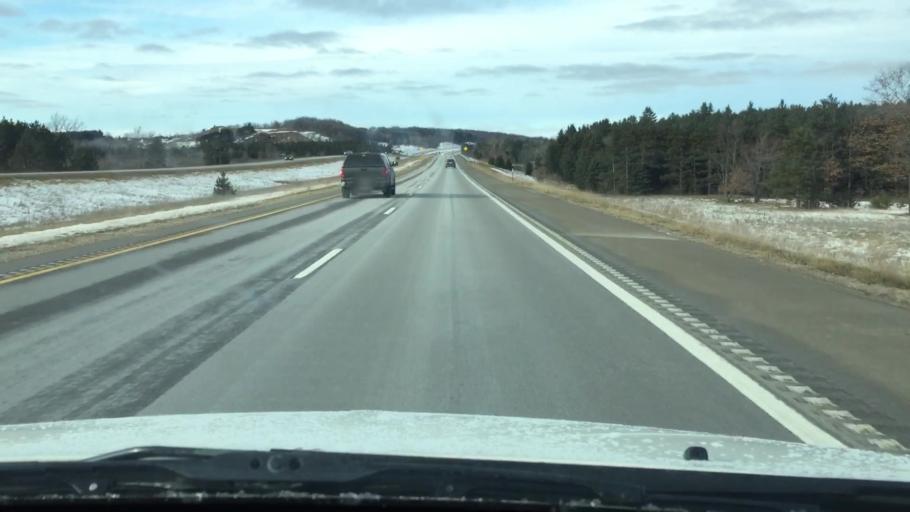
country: US
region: Michigan
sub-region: Wexford County
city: Manton
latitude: 44.4240
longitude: -85.3849
